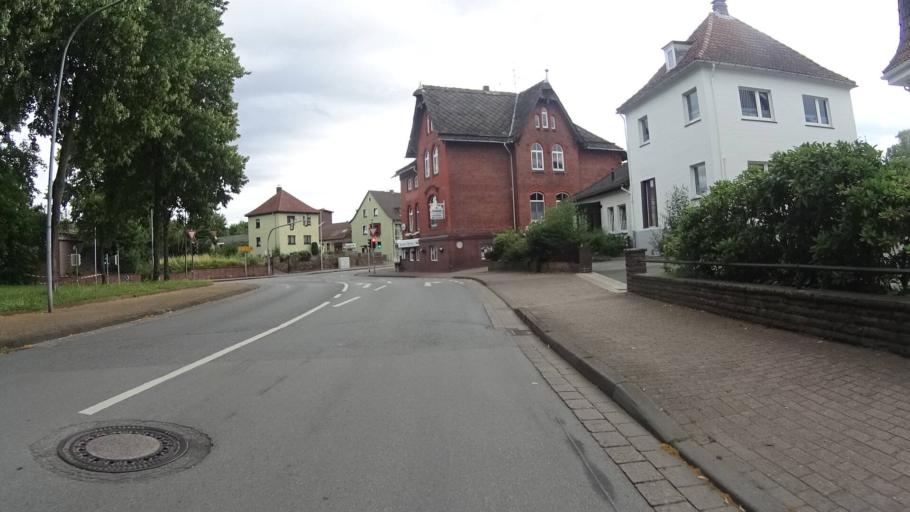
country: DE
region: Lower Saxony
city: Holzminden
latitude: 51.8271
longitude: 9.4583
